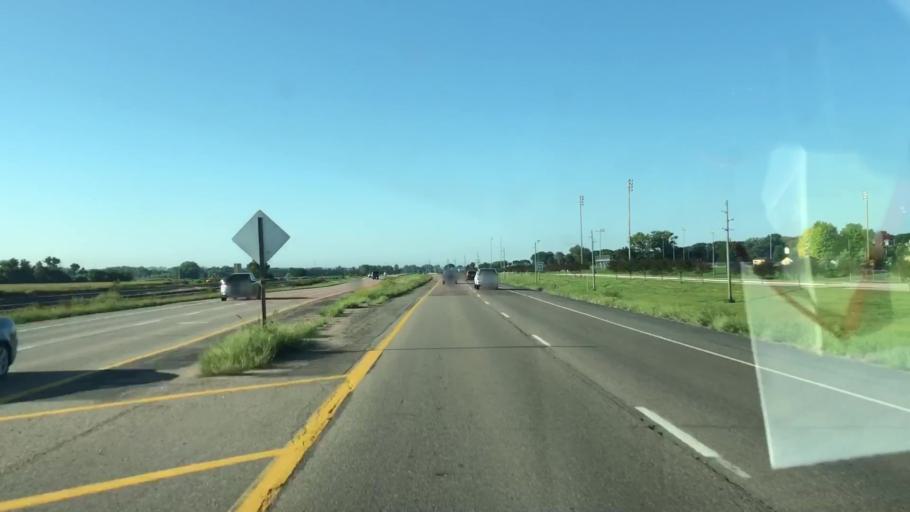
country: US
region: Iowa
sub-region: Woodbury County
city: Sioux City
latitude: 42.6231
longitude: -96.2930
